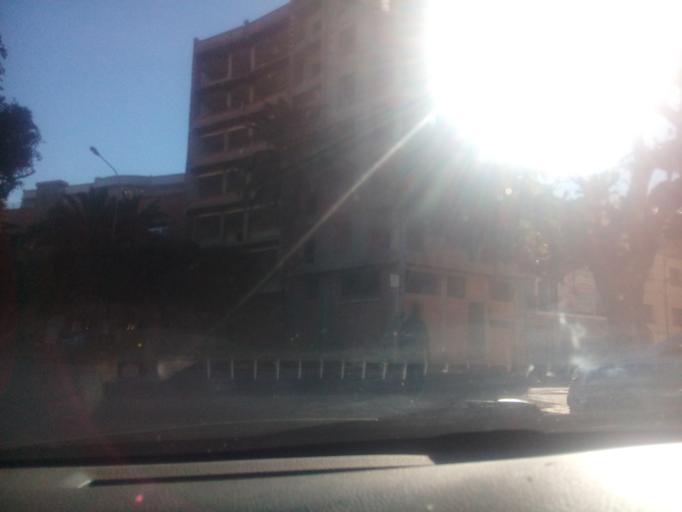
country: DZ
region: Oran
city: Oran
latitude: 35.7112
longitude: -0.6203
